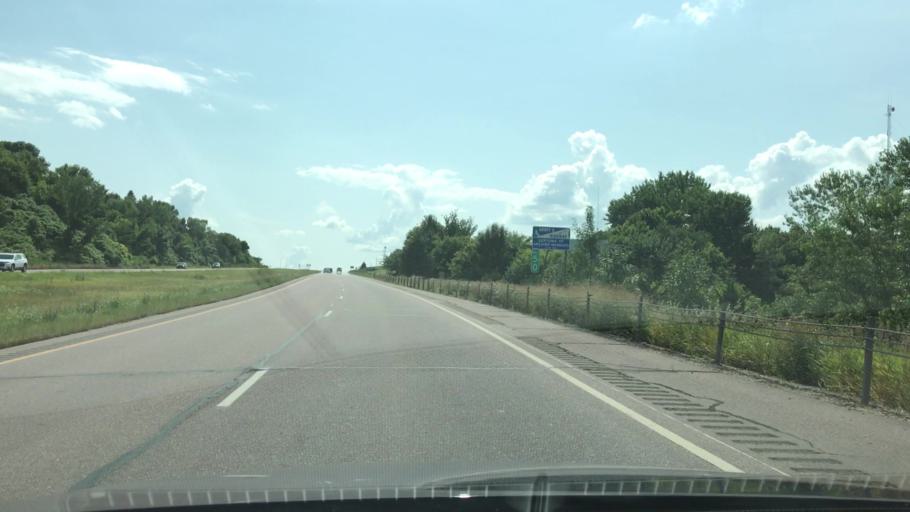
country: US
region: Minnesota
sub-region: Nicollet County
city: North Mankato
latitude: 44.1508
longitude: -94.0755
